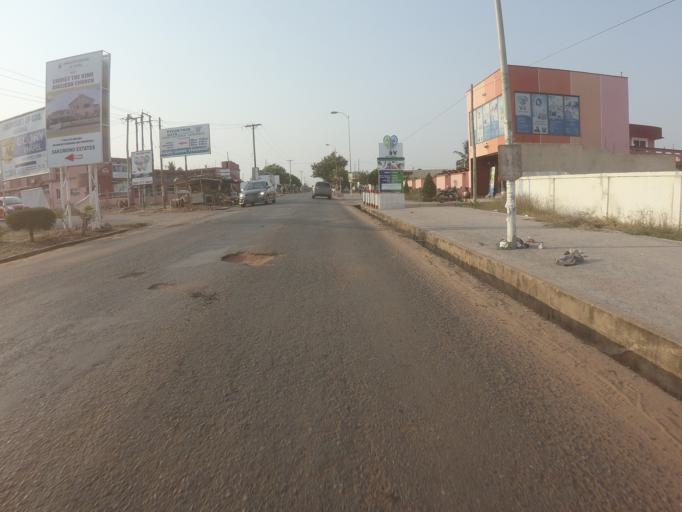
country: GH
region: Greater Accra
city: Nungua
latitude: 5.6182
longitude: -0.0535
